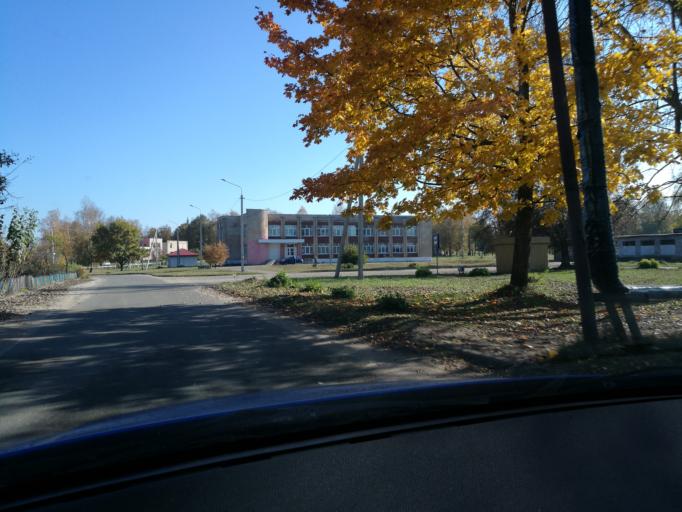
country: BY
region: Minsk
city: Krupki
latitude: 54.1050
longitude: 29.2079
